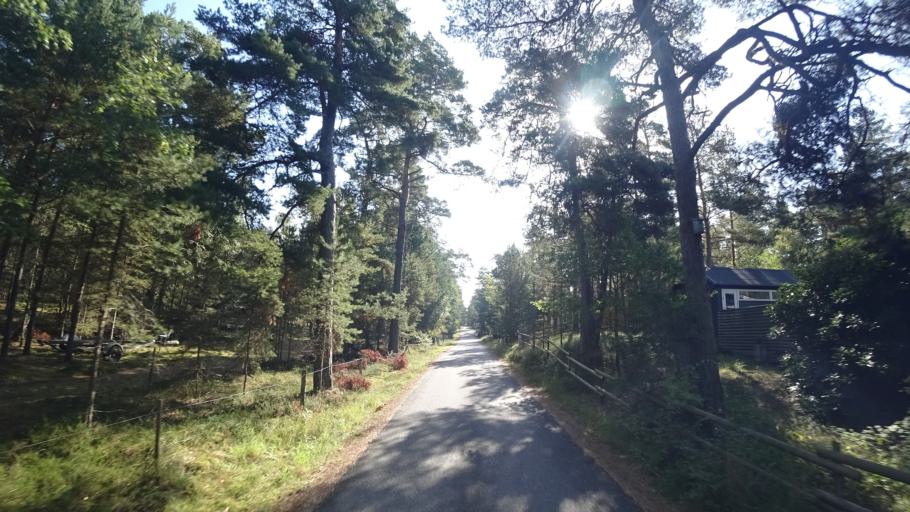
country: SE
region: Skane
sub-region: Kristianstads Kommun
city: Ahus
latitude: 55.9171
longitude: 14.3080
